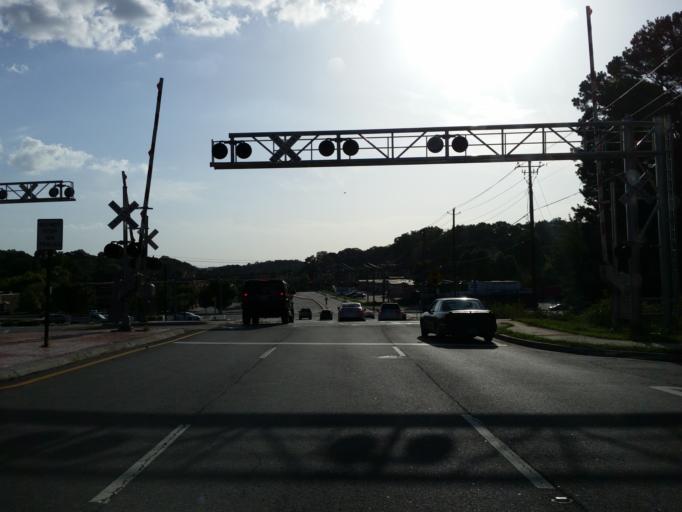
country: US
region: Georgia
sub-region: Cherokee County
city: Woodstock
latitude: 34.0691
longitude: -84.5199
